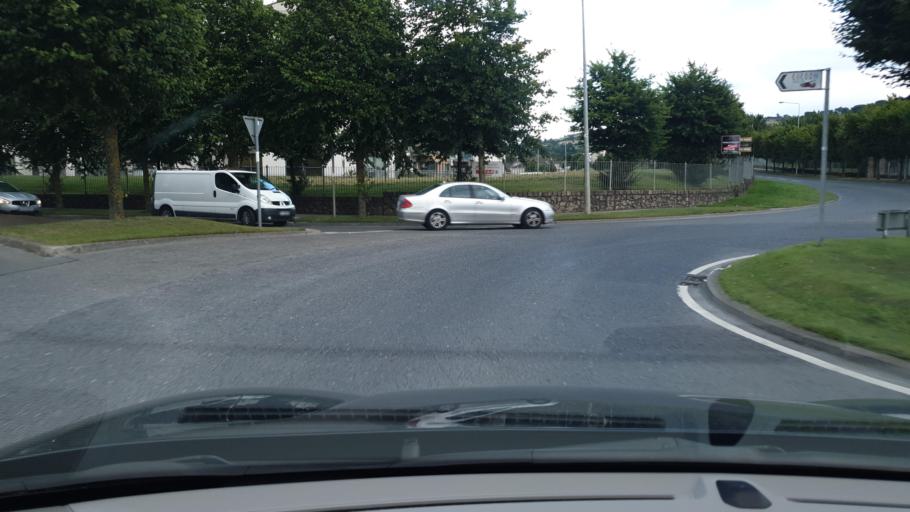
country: IE
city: Jobstown
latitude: 53.2784
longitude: -6.4201
